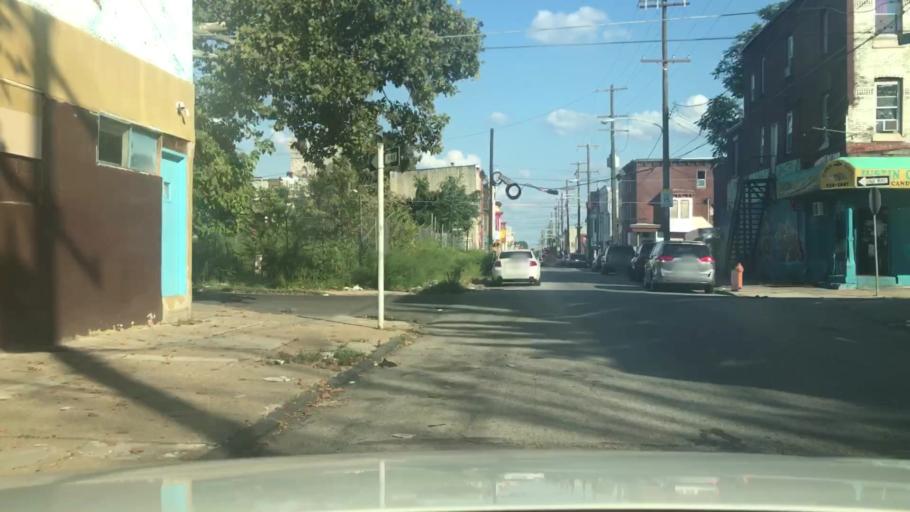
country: US
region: Pennsylvania
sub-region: Philadelphia County
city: Philadelphia
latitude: 39.9893
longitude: -75.1424
